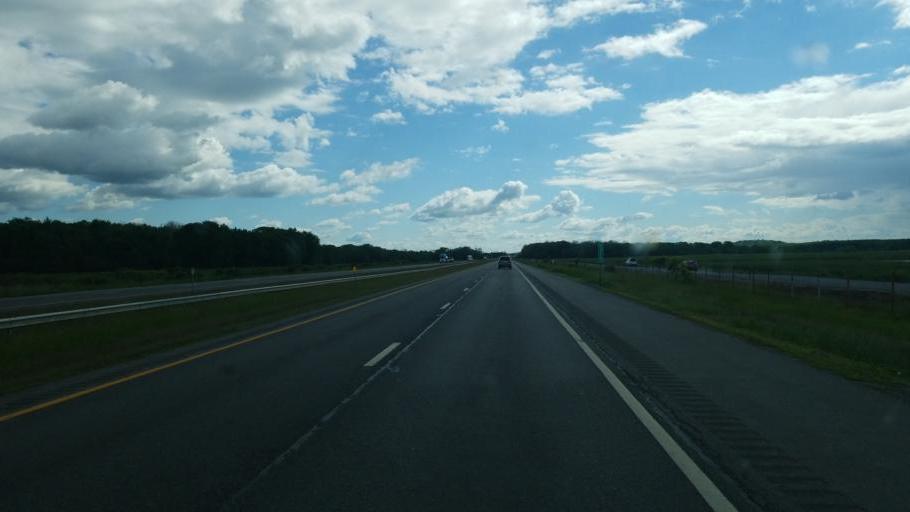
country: US
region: New York
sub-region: Seneca County
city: Bridgeport
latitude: 42.9912
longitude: -76.7529
